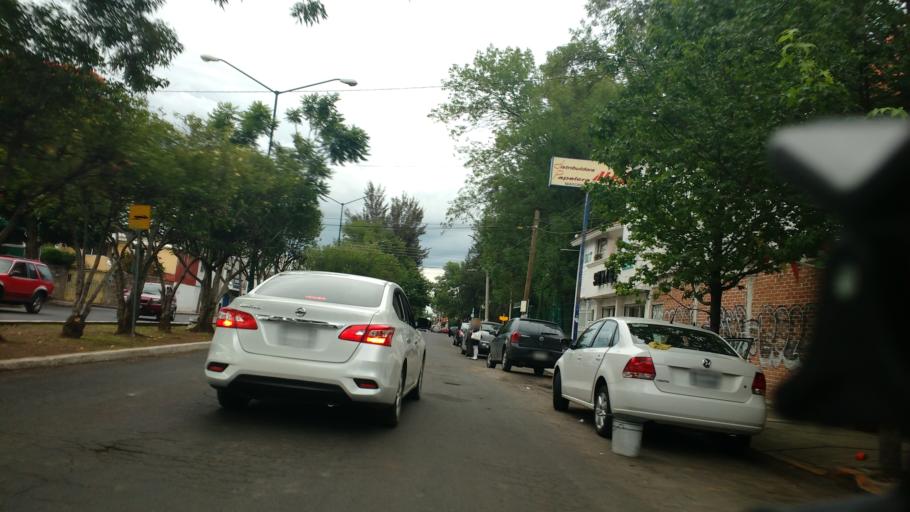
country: MX
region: Michoacan
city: Morelia
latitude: 19.6831
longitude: -101.1738
